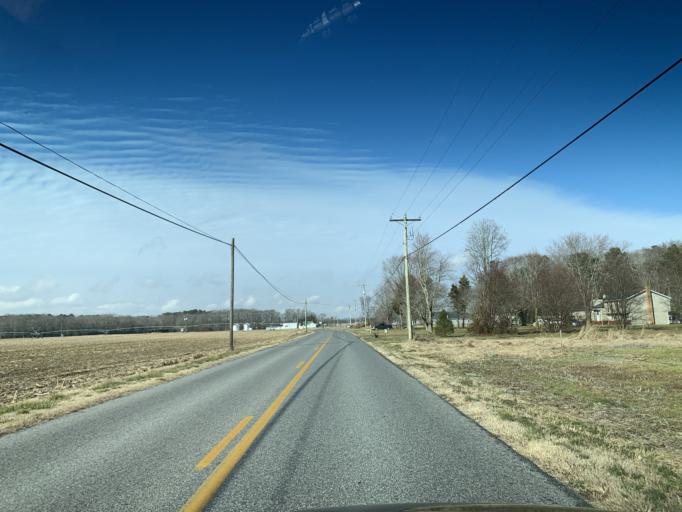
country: US
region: Maryland
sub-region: Worcester County
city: Ocean Pines
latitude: 38.4281
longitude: -75.1742
